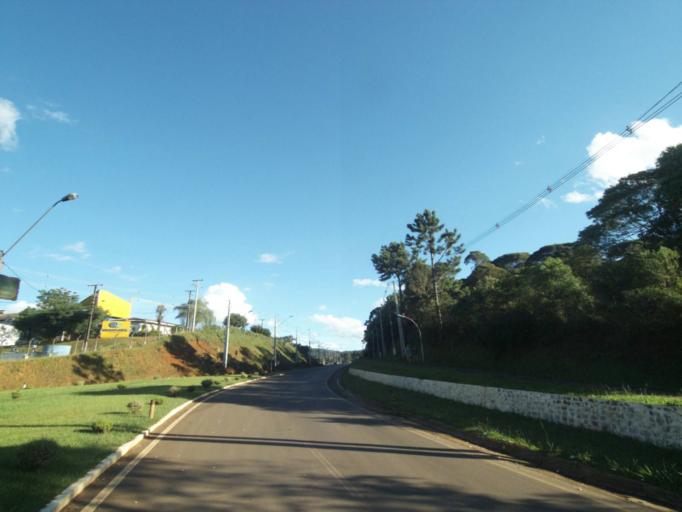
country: BR
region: Parana
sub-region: Uniao Da Vitoria
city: Uniao da Vitoria
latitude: -26.1534
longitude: -51.5432
